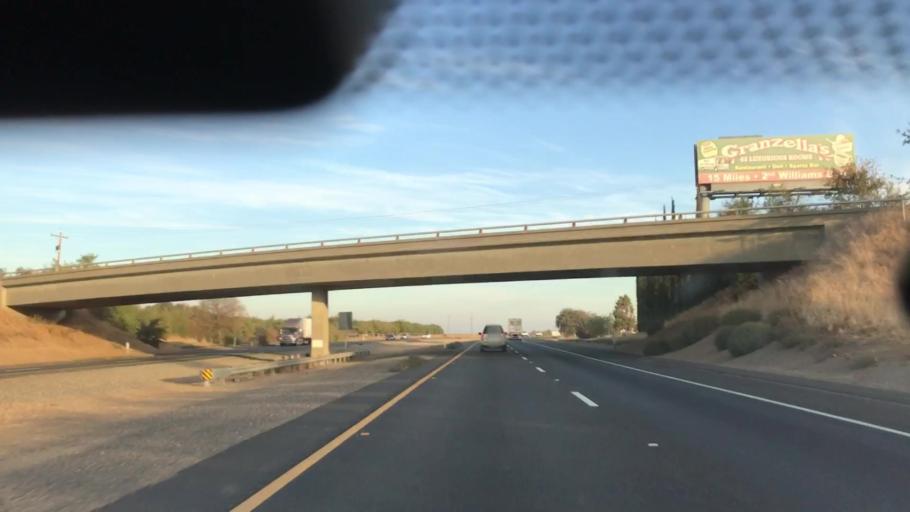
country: US
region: California
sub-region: Colusa County
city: Arbuckle
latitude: 38.9656
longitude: -122.0254
